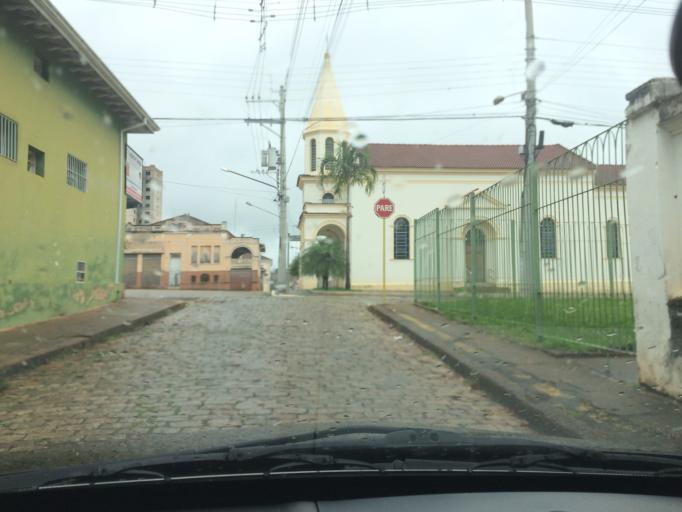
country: BR
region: Sao Paulo
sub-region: Casa Branca
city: Casa Branca
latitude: -21.7708
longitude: -47.0877
